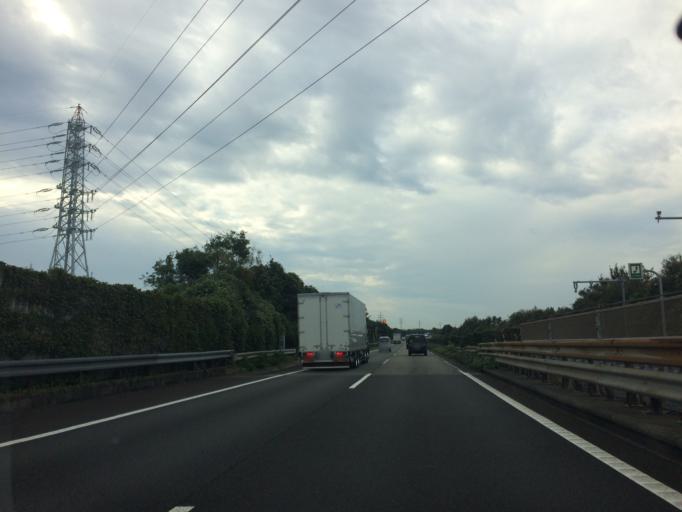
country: JP
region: Shizuoka
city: Fujieda
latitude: 34.8520
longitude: 138.2821
